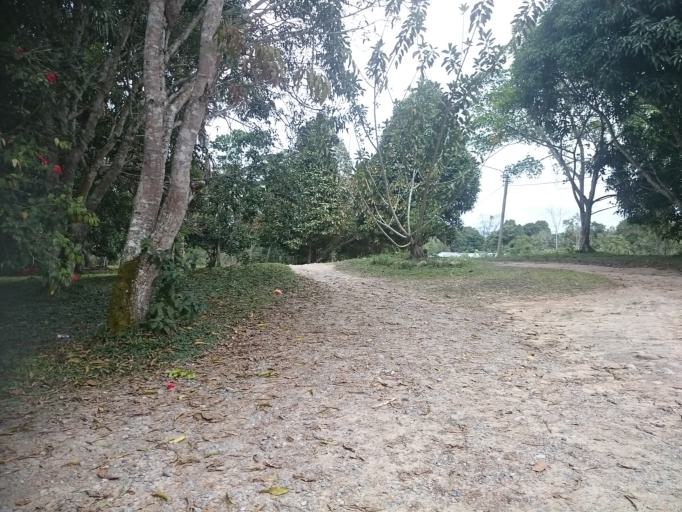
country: PE
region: San Martin
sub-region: Provincia de Rioja
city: Rioja
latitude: -6.0564
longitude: -77.1771
